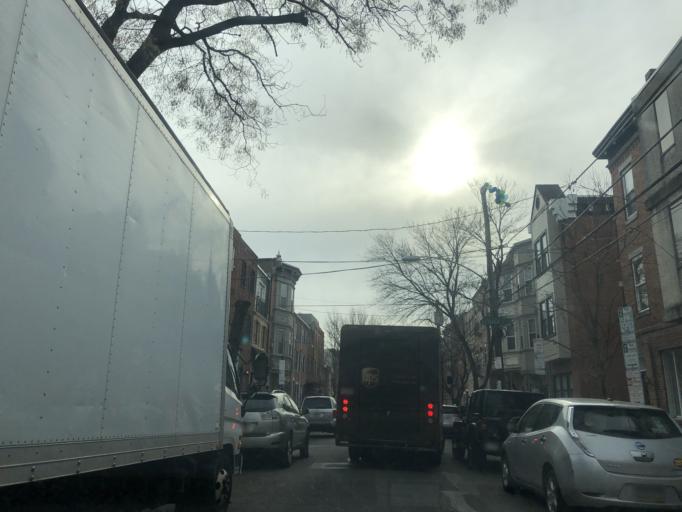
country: US
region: Pennsylvania
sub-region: Philadelphia County
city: Philadelphia
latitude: 39.9400
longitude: -75.1528
